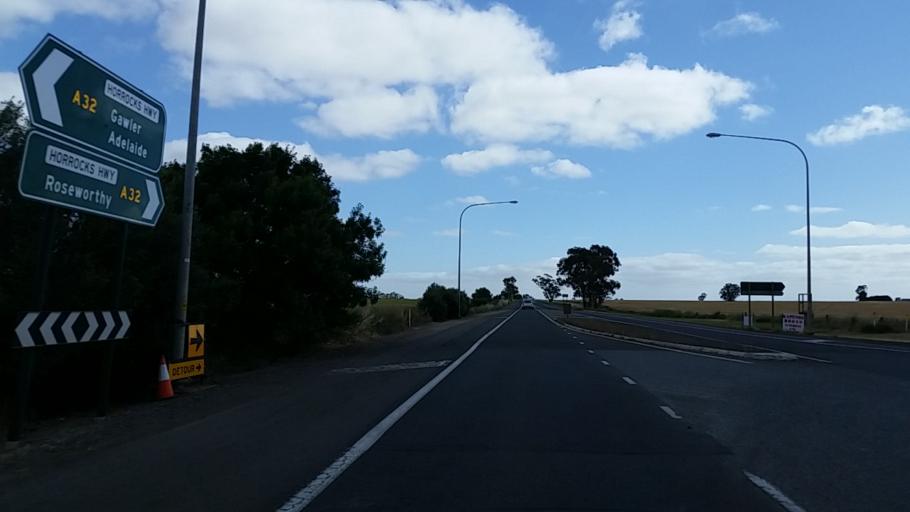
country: AU
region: South Australia
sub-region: Light
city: Willaston
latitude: -34.5667
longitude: 138.7462
